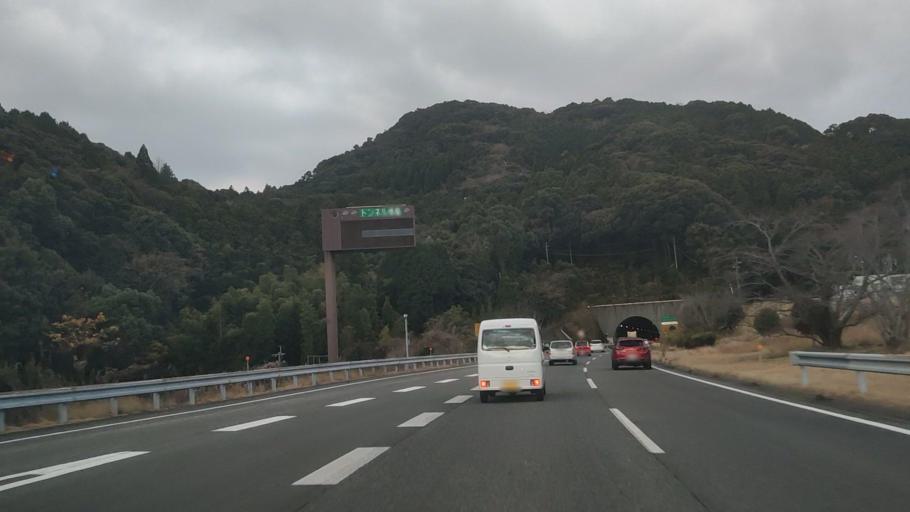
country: JP
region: Nagasaki
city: Obita
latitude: 32.8147
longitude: 129.9452
